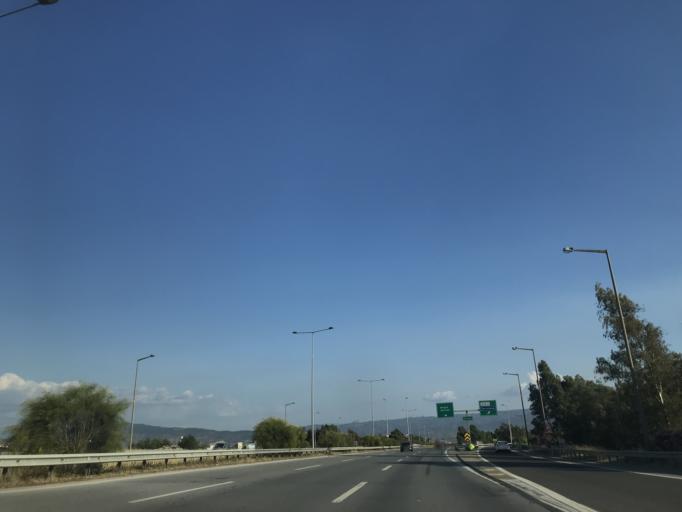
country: TR
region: Aydin
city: Aydin
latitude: 37.8495
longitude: 27.8069
